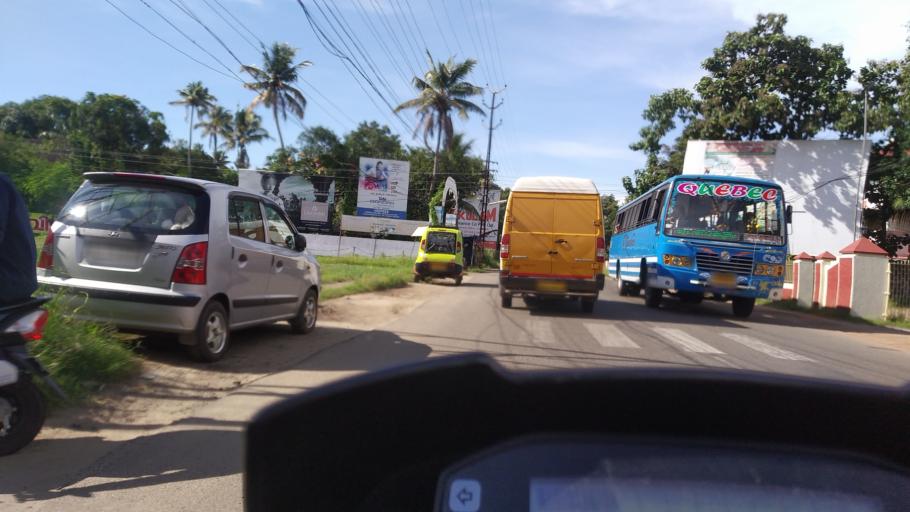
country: IN
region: Kerala
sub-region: Ernakulam
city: Elur
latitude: 10.0333
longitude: 76.2211
